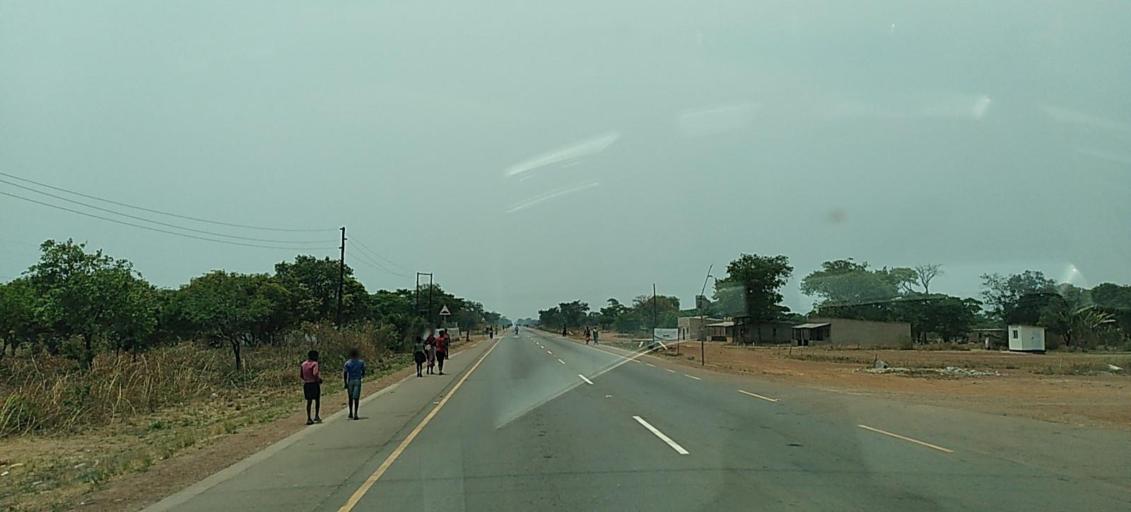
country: CD
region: Katanga
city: Kipushi
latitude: -12.3351
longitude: 27.0660
